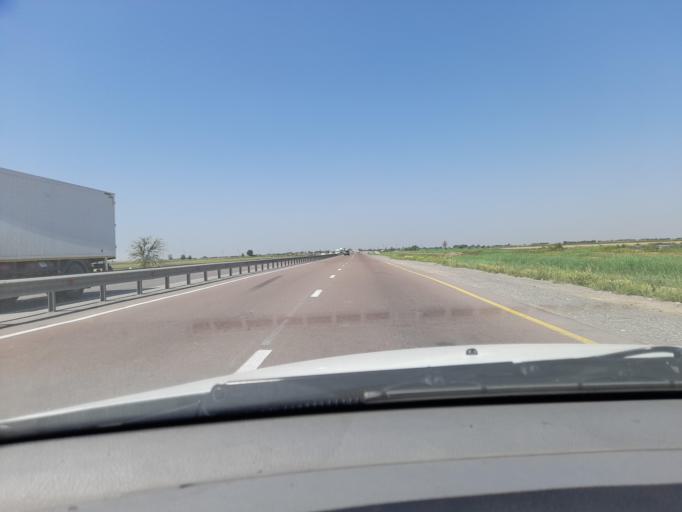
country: KZ
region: Ongtustik Qazaqstan
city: Myrzakent
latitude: 40.5174
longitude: 68.4760
